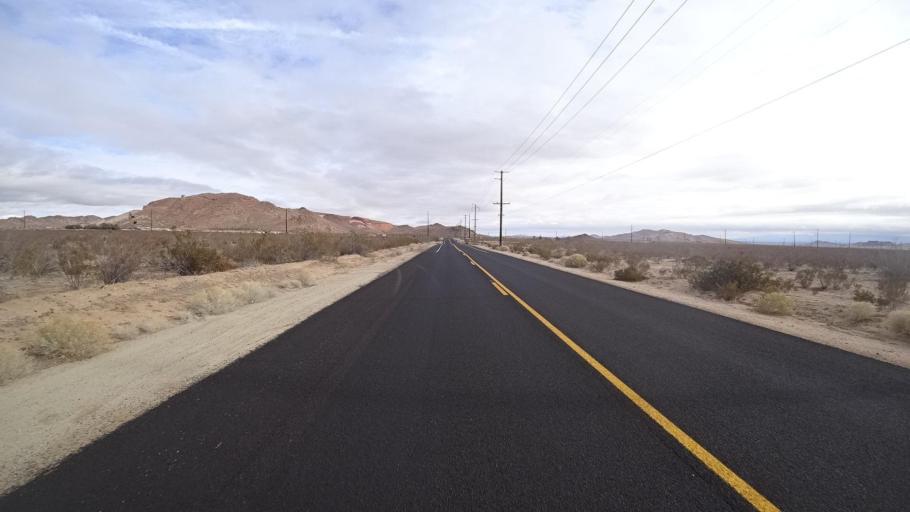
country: US
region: California
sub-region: Kern County
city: Rosamond
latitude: 34.9509
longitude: -118.2977
